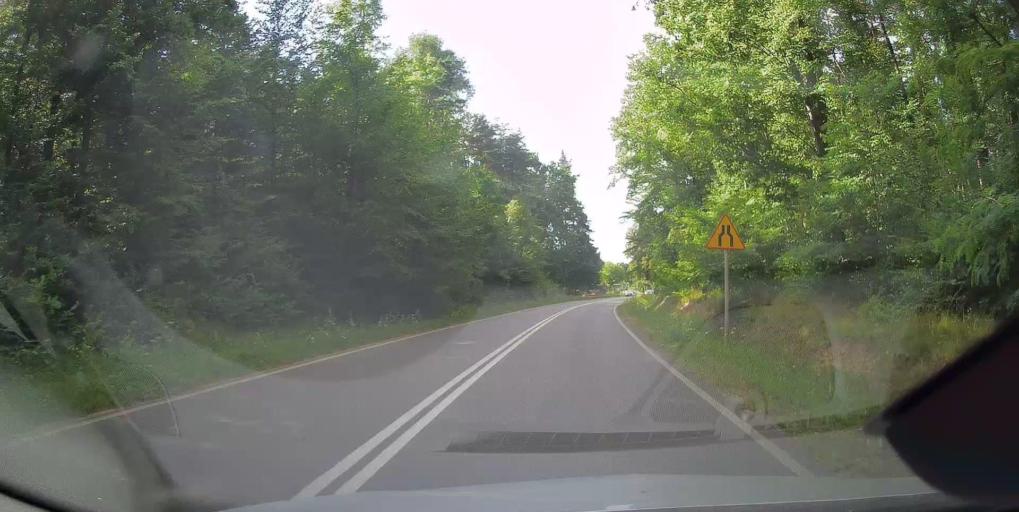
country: PL
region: Swietokrzyskie
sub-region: Powiat skarzyski
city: Laczna
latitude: 50.9965
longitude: 20.8526
